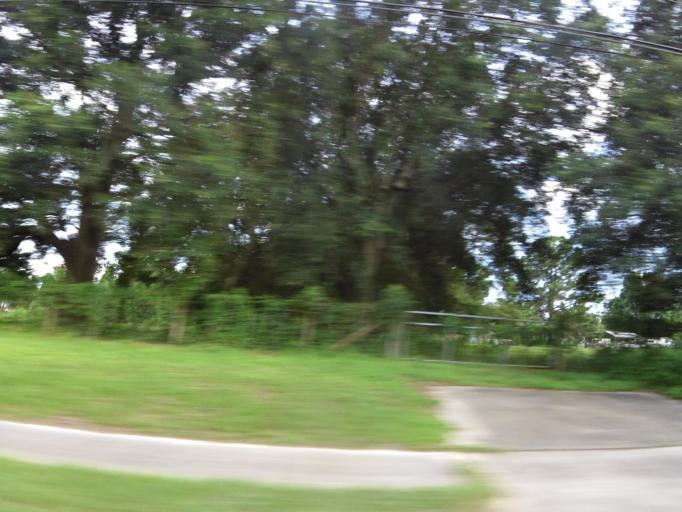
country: US
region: Florida
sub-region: Nassau County
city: Nassau Village-Ratliff
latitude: 30.3715
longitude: -81.8010
